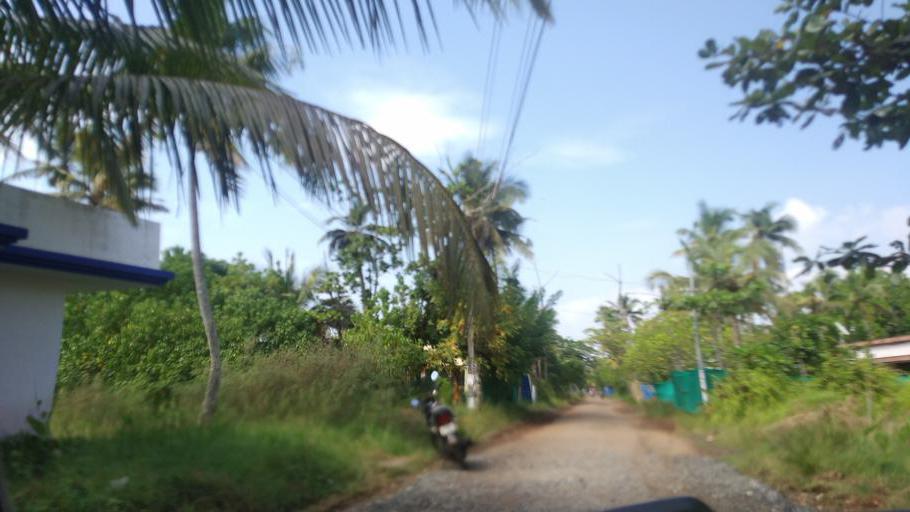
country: IN
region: Kerala
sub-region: Ernakulam
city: Elur
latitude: 10.0656
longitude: 76.1993
